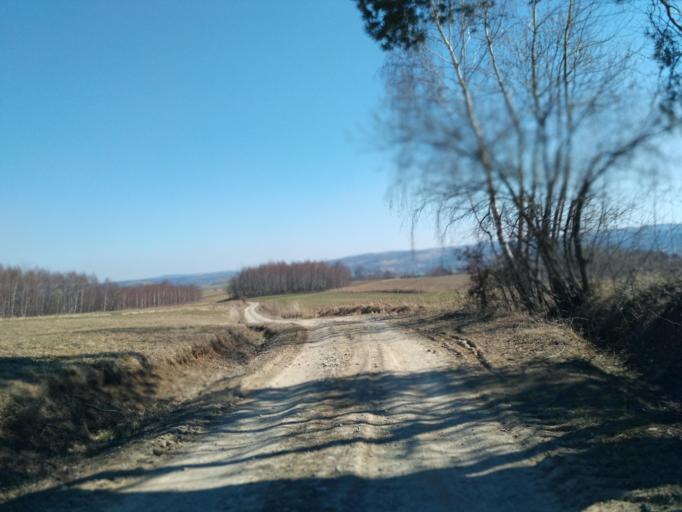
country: PL
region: Subcarpathian Voivodeship
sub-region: Powiat ropczycko-sedziszowski
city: Niedzwiada
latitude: 49.9541
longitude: 21.5565
